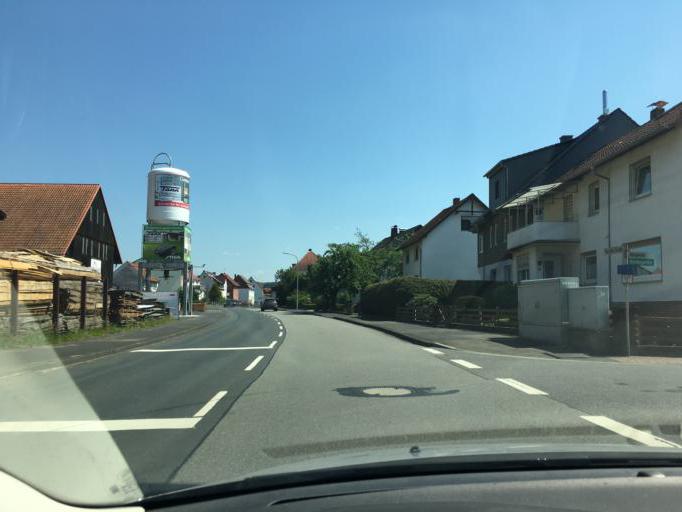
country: DE
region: Hesse
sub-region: Regierungsbezirk Kassel
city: Ronshausen
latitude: 50.9500
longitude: 9.8529
